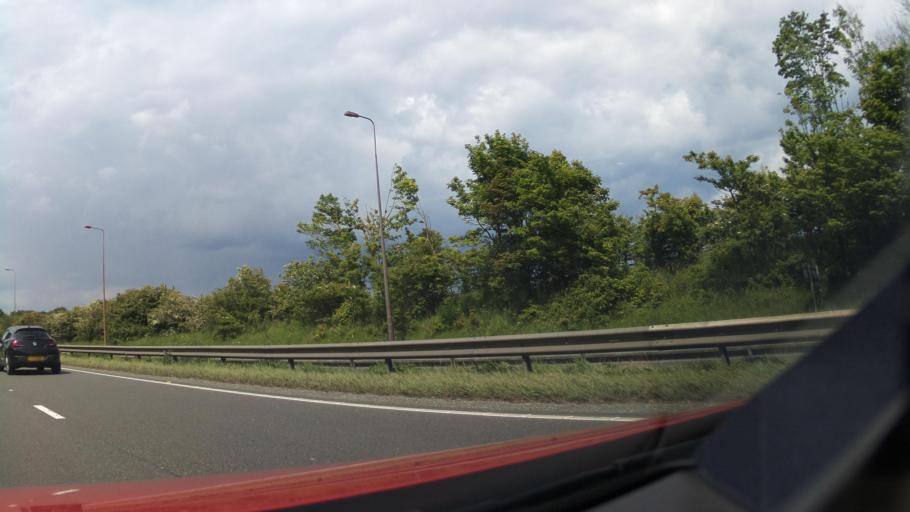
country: GB
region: England
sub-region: County Durham
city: Peterlee
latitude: 54.7226
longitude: -1.3310
